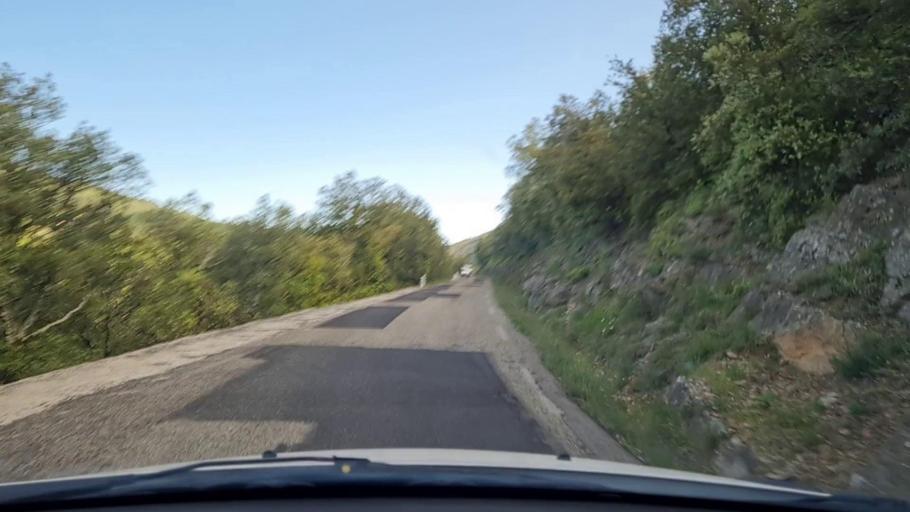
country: FR
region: Languedoc-Roussillon
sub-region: Departement du Gard
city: Les Salles-du-Gardon
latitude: 44.1793
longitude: 4.0202
